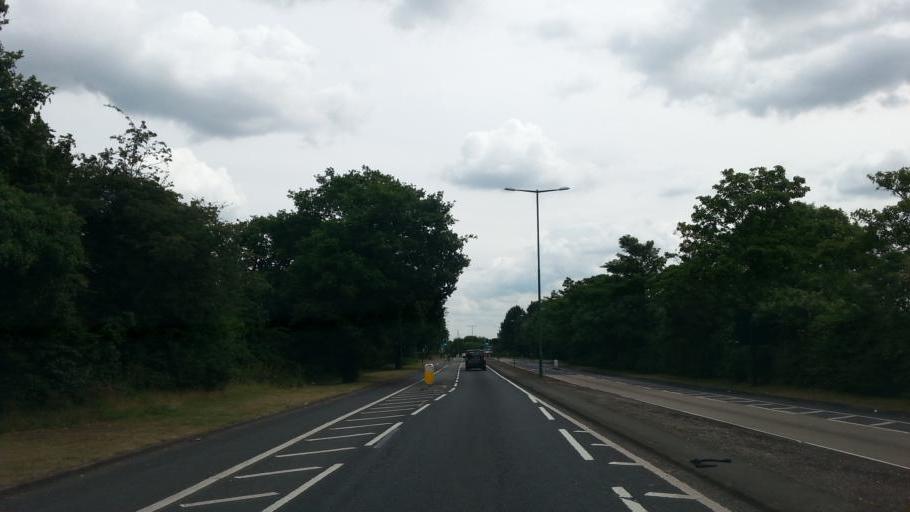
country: GB
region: England
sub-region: Solihull
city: Chelmsley Wood
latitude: 52.4777
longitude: -1.7254
